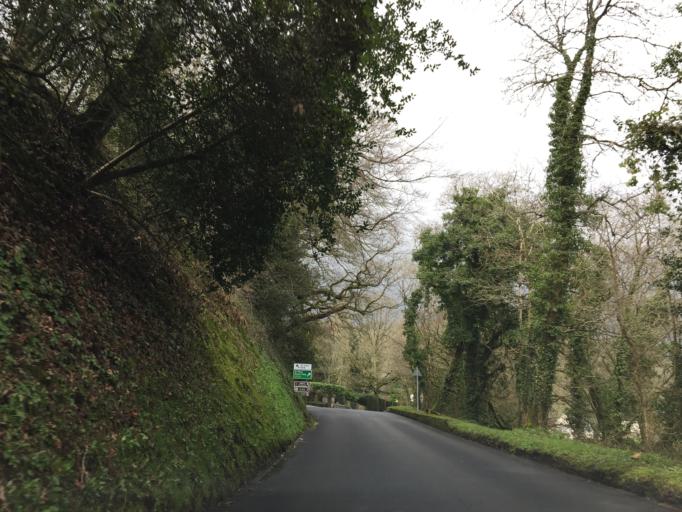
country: JE
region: St Helier
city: Saint Helier
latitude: 49.2187
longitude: -2.1739
